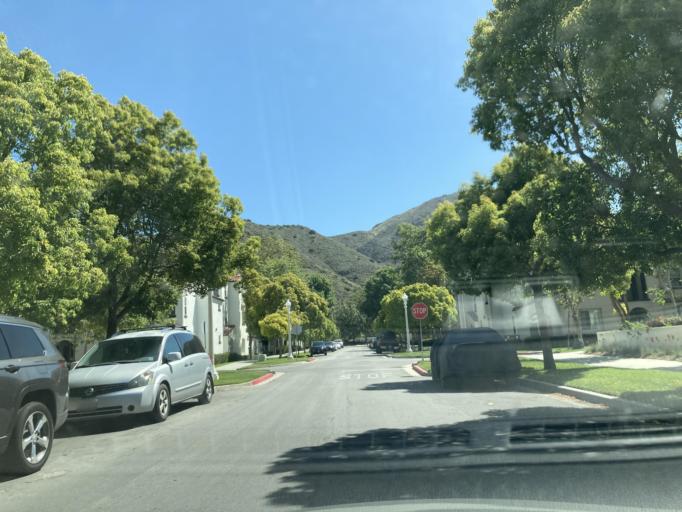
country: US
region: California
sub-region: Ventura County
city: Camarillo
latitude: 34.1641
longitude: -119.0355
